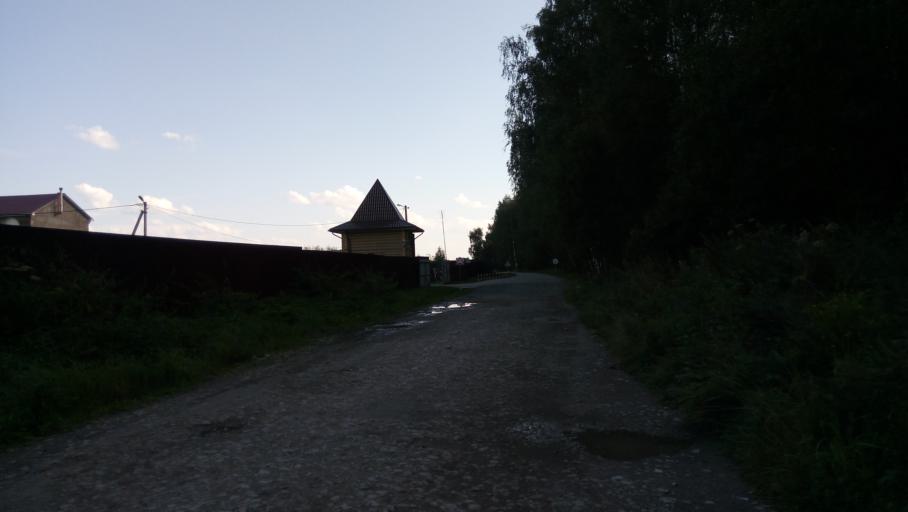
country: RU
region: Moskovskaya
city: Proletarskiy
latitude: 55.0500
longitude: 37.4007
